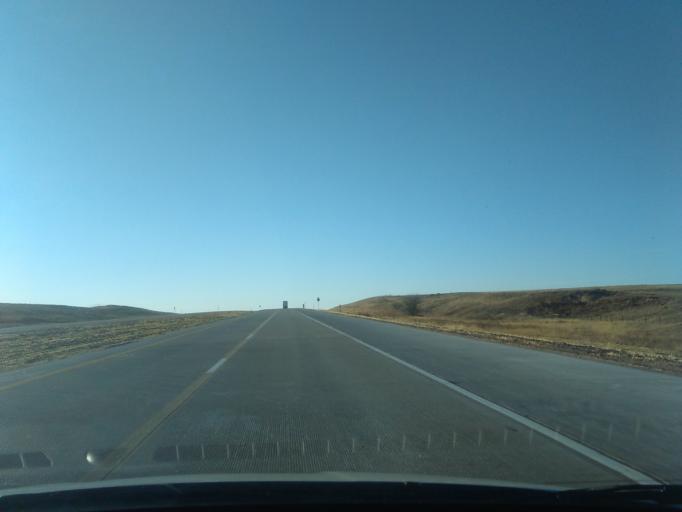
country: US
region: Nebraska
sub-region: Deuel County
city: Chappell
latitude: 41.1137
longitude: -102.6387
